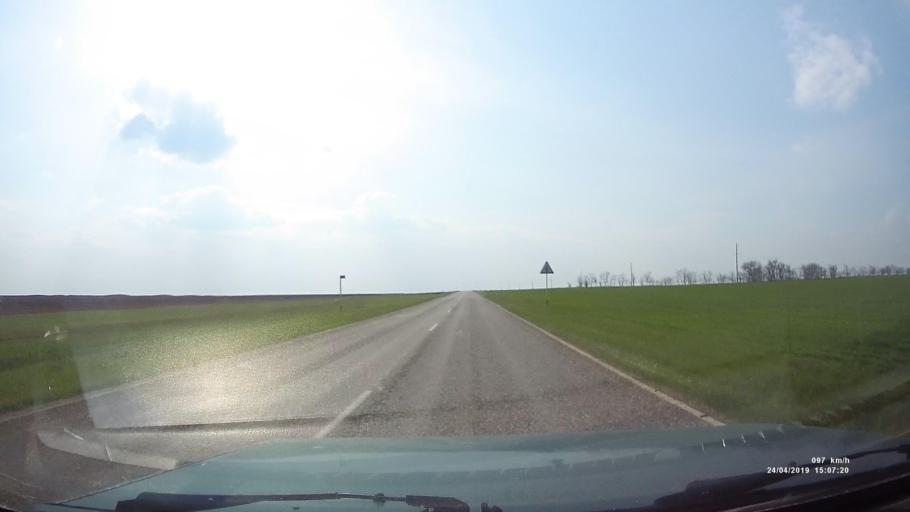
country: RU
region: Rostov
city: Remontnoye
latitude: 46.5595
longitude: 43.4073
